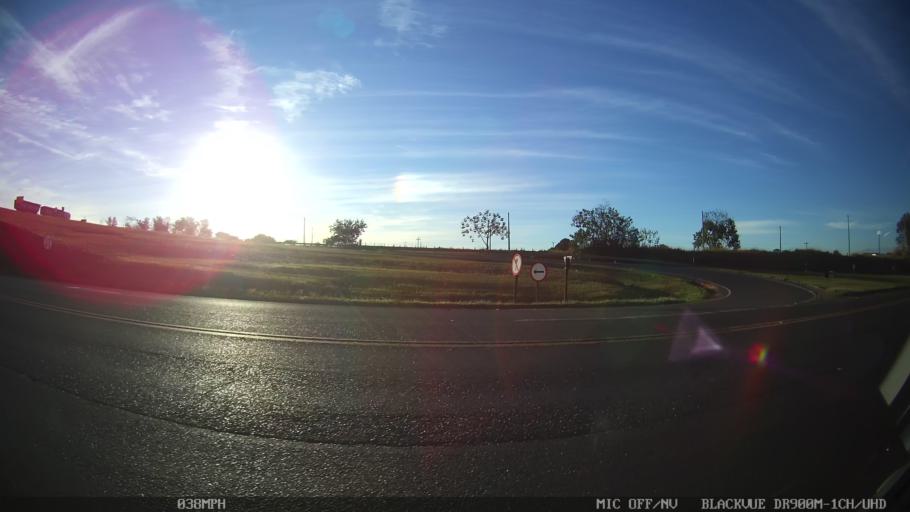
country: BR
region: Sao Paulo
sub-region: Guapiacu
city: Guapiacu
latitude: -20.9905
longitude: -49.2045
